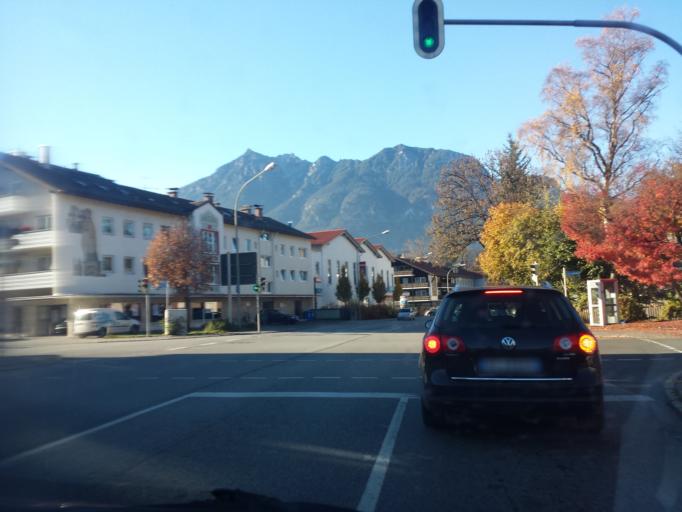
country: DE
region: Bavaria
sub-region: Upper Bavaria
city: Garmisch-Partenkirchen
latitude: 47.4914
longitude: 11.1087
